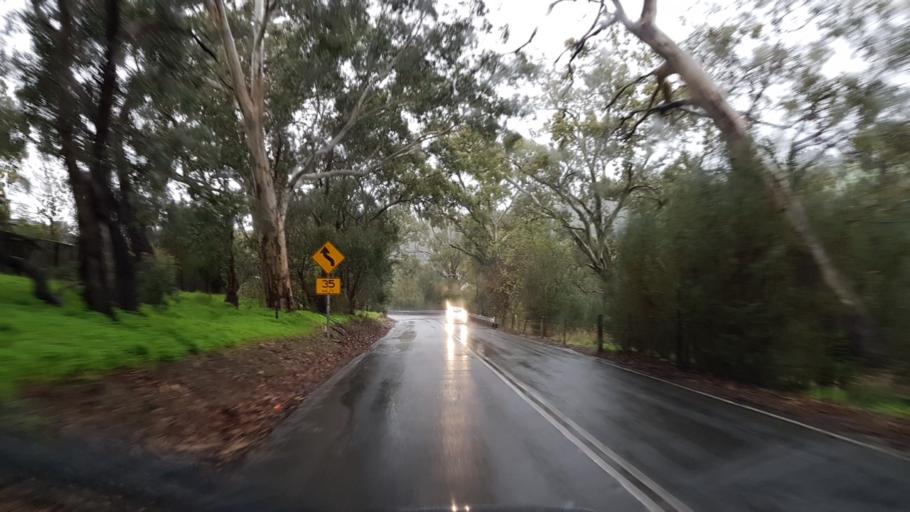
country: AU
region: South Australia
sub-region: Onkaparinga
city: Craigburn Farm
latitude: -35.0564
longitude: 138.6200
